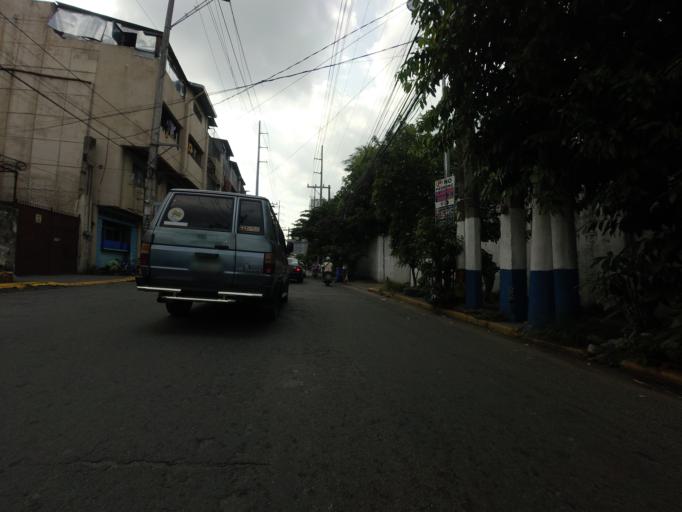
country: PH
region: Metro Manila
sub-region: City of Manila
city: Quiapo
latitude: 14.5808
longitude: 120.9917
